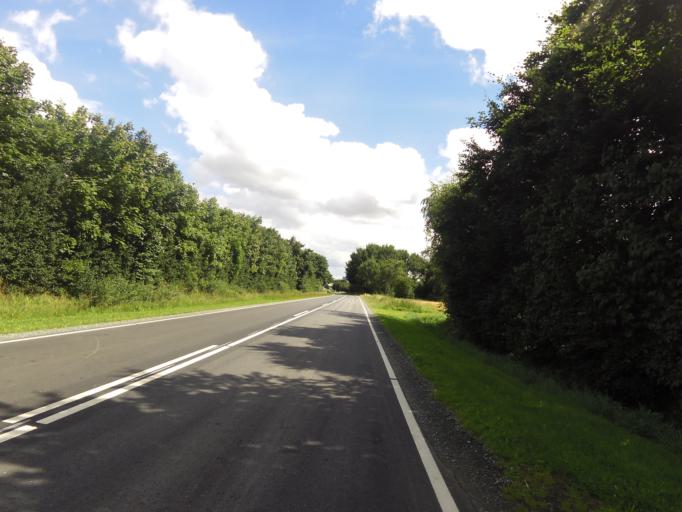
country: DK
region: South Denmark
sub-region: Haderslev Kommune
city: Vojens
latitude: 55.2805
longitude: 9.2001
